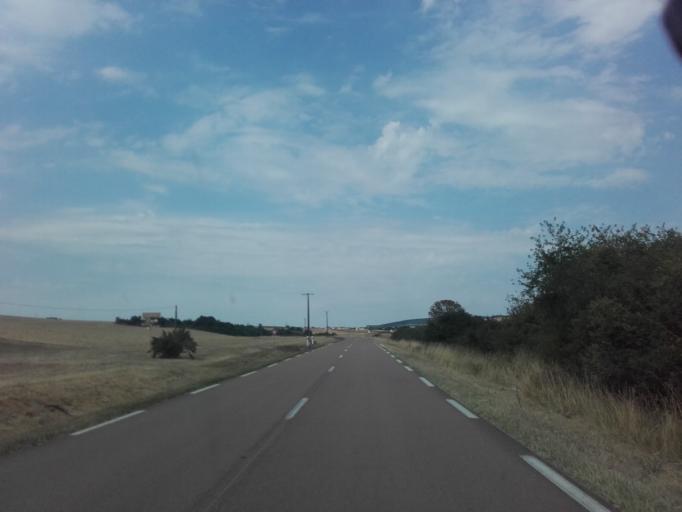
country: FR
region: Bourgogne
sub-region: Departement de l'Yonne
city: Chablis
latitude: 47.7878
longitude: 3.8041
